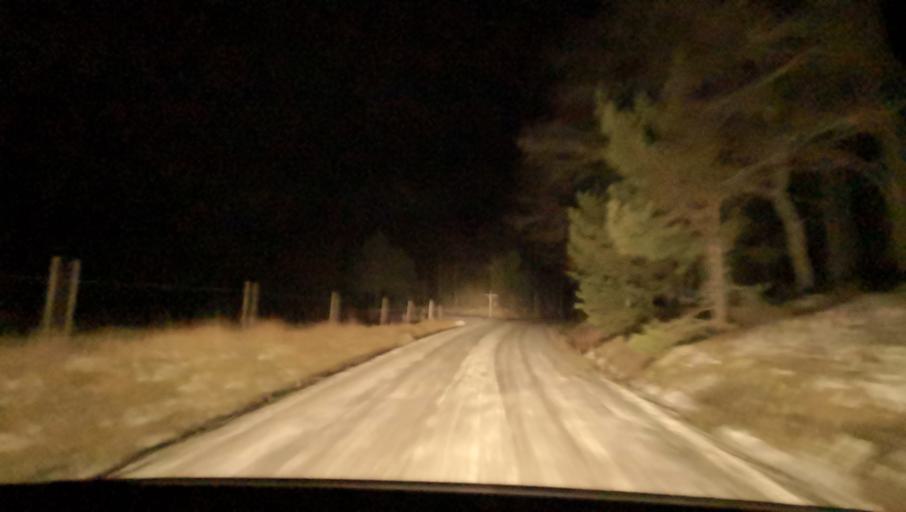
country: SE
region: Stockholm
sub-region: Nacka Kommun
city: Alta
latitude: 59.2875
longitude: 18.2205
